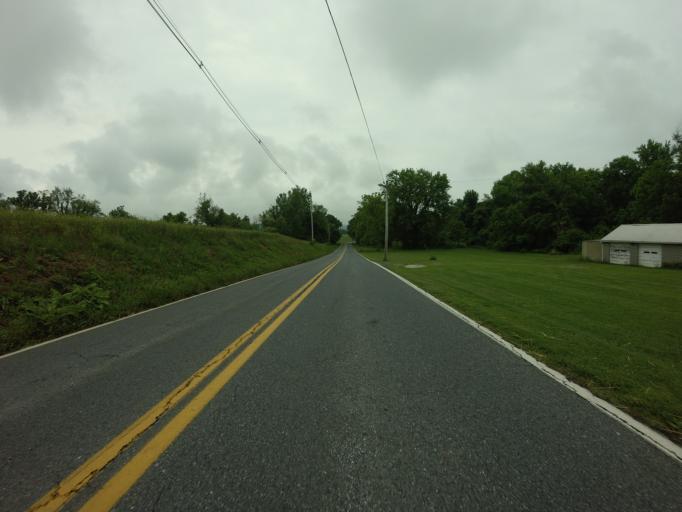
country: US
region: Maryland
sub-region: Frederick County
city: Jefferson
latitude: 39.3564
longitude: -77.5319
